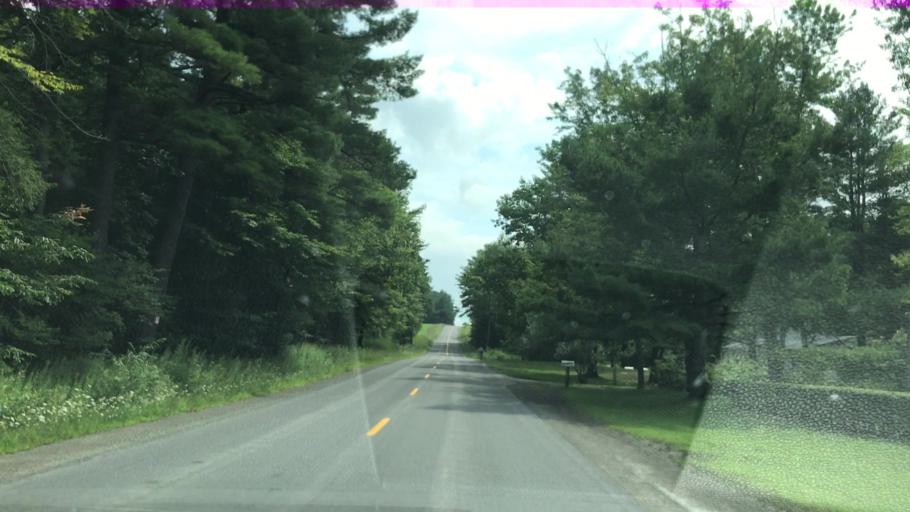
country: US
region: New York
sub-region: Steuben County
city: Sylvan Beach
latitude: 42.5114
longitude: -77.2299
